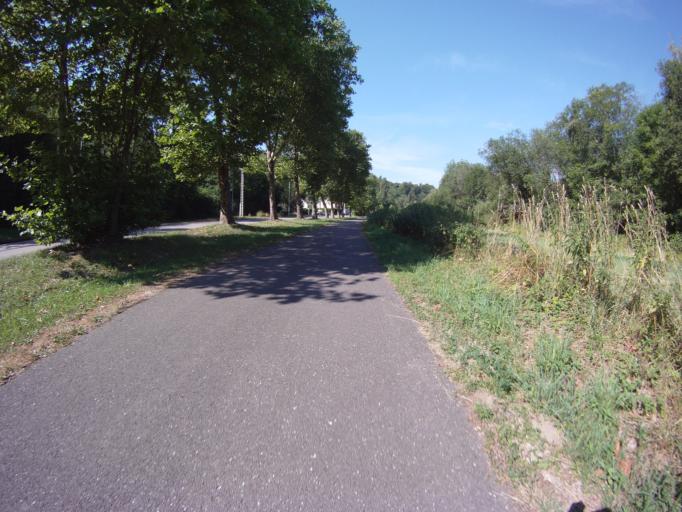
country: FR
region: Lorraine
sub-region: Departement de Meurthe-et-Moselle
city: Liverdun
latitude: 48.7473
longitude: 6.0766
